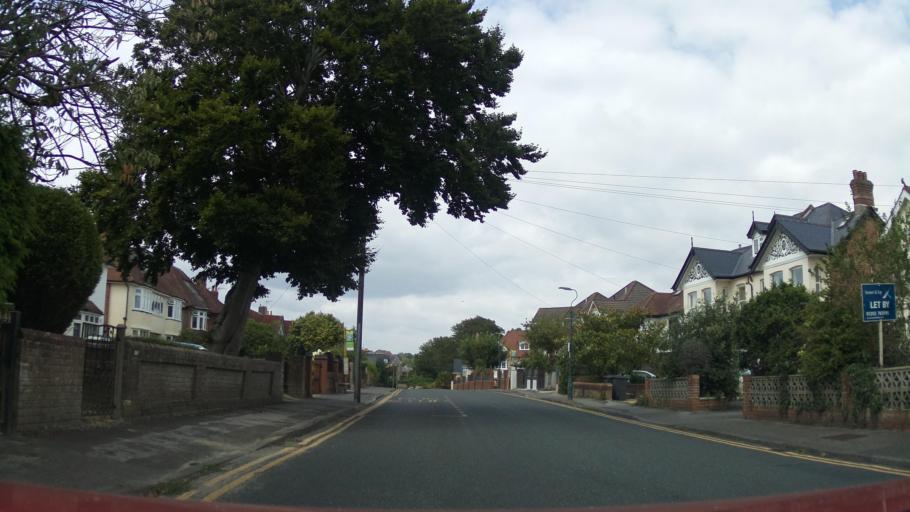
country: GB
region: England
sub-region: Bournemouth
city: Bournemouth
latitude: 50.7144
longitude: -1.9039
